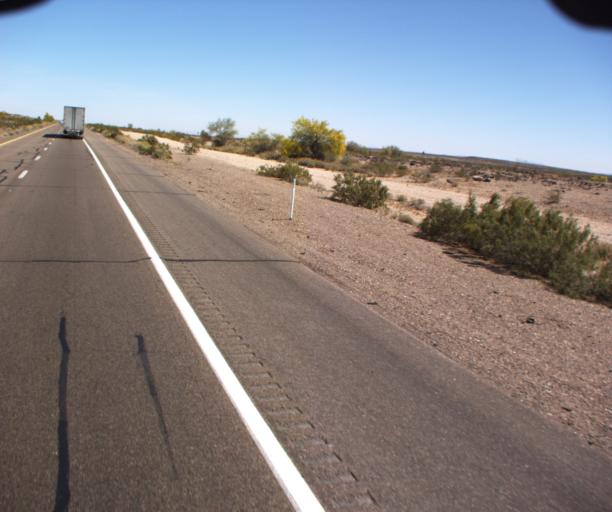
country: US
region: Arizona
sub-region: Maricopa County
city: Gila Bend
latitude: 32.8687
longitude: -113.1448
